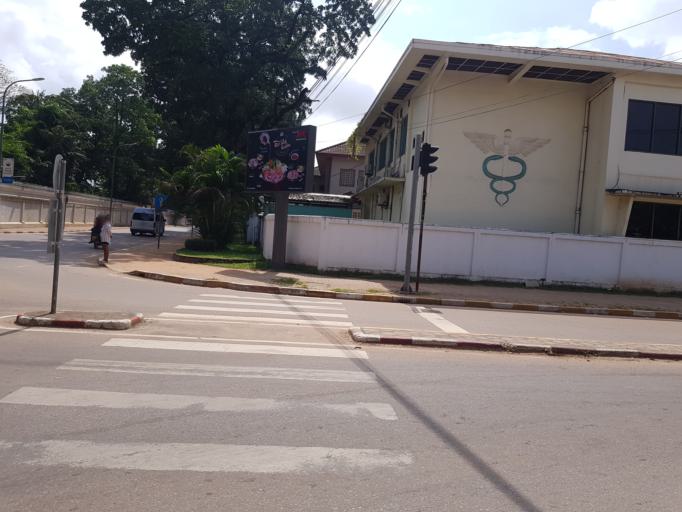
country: LA
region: Vientiane
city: Vientiane
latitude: 17.9616
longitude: 102.6120
